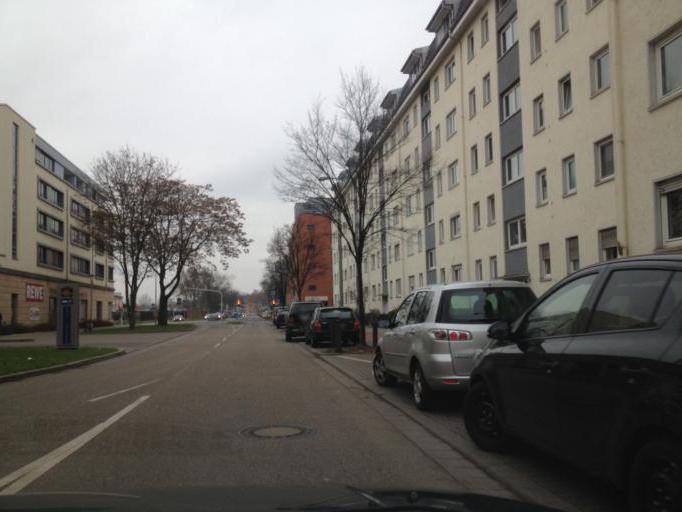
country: DE
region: Baden-Wuerttemberg
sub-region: Karlsruhe Region
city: Mannheim
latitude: 49.4734
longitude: 8.4712
